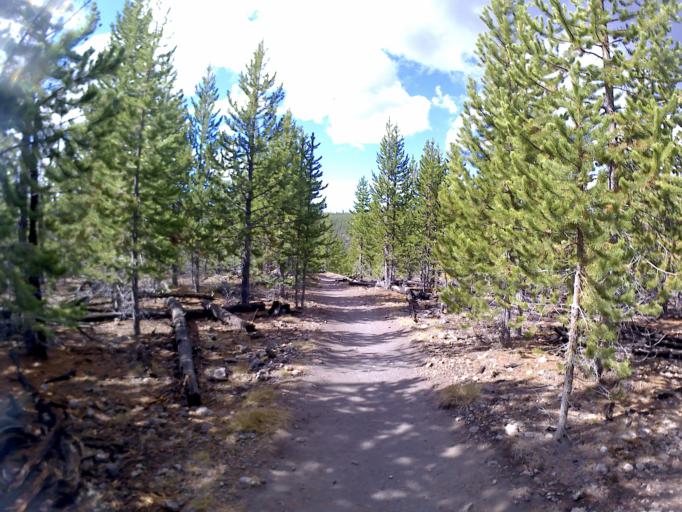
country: US
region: Montana
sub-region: Gallatin County
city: West Yellowstone
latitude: 44.4865
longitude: -110.8702
